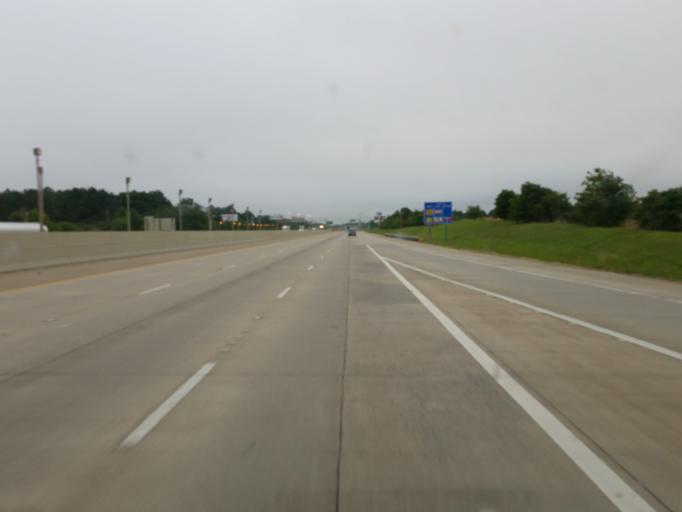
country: US
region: Louisiana
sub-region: Caddo Parish
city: Shreveport
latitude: 32.4573
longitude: -93.8405
